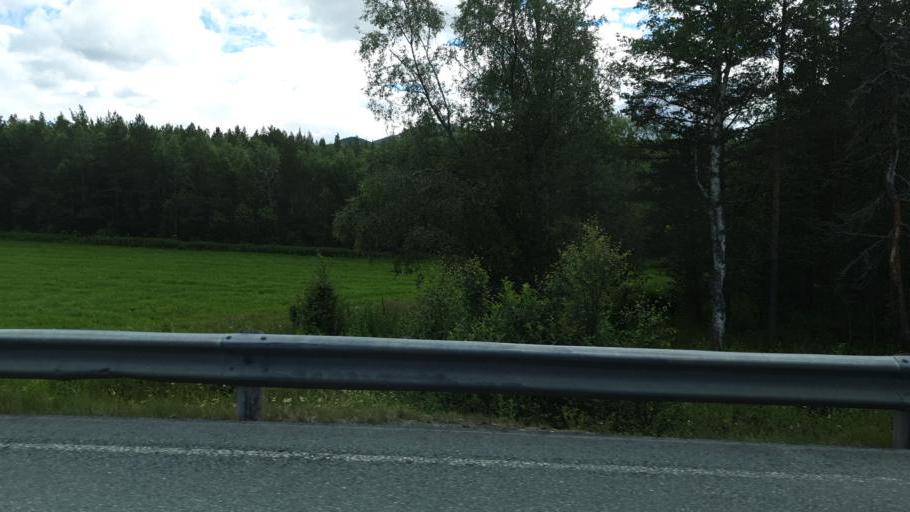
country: NO
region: Sor-Trondelag
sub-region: Oppdal
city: Oppdal
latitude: 62.6524
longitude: 9.8641
